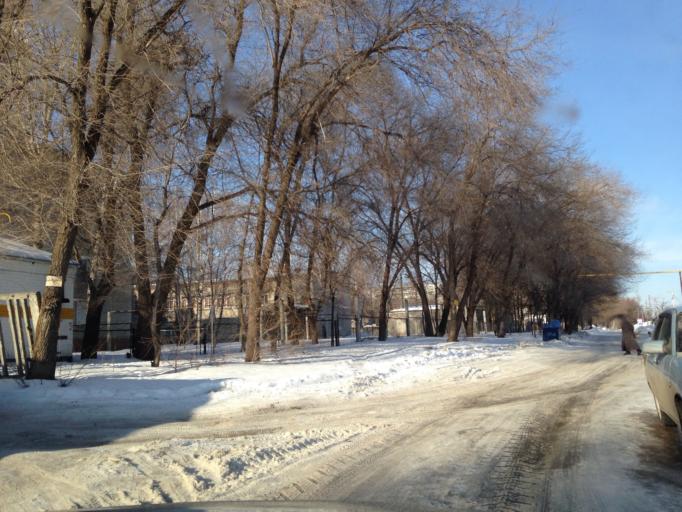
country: RU
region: Ulyanovsk
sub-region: Ulyanovskiy Rayon
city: Ulyanovsk
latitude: 54.3396
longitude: 48.5455
